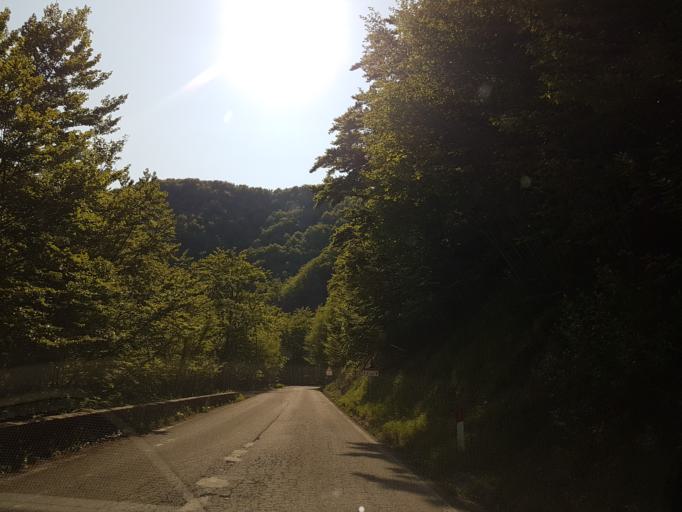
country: IT
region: Emilia-Romagna
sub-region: Forli-Cesena
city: San Piero in Bagno
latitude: 43.8087
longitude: 11.9197
